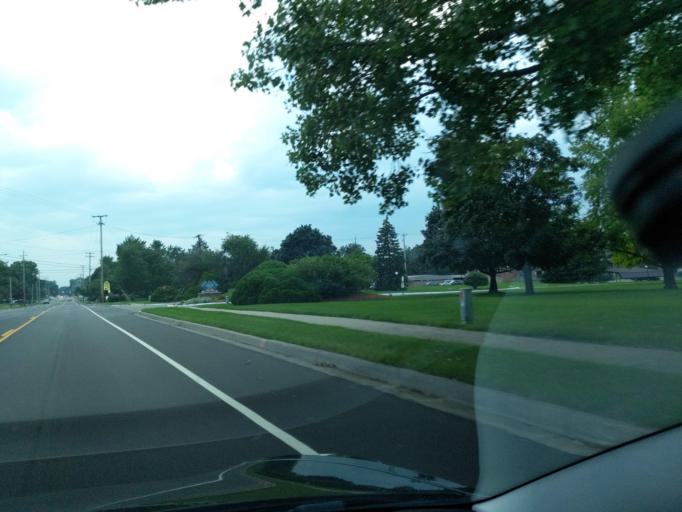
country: US
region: Michigan
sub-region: Eaton County
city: Waverly
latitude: 42.7338
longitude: -84.6261
